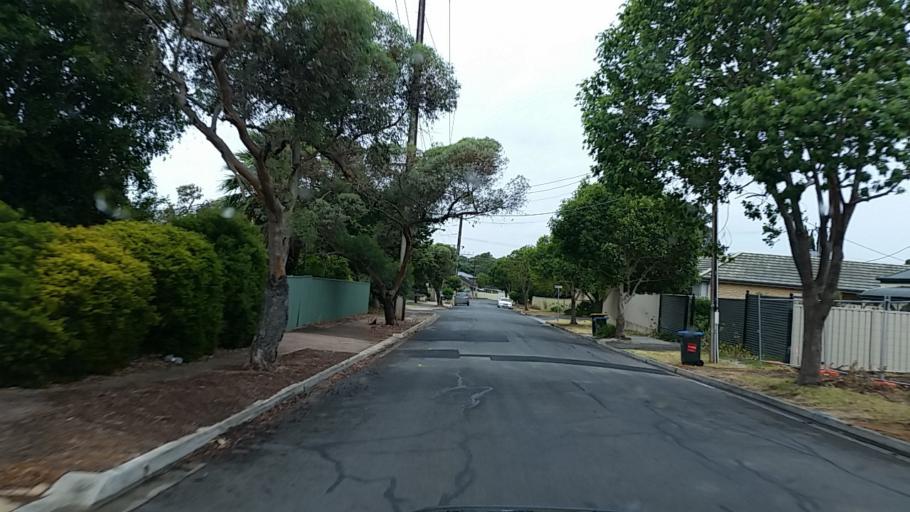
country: AU
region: South Australia
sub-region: Campbelltown
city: Campbelltown
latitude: -34.8959
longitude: 138.6820
